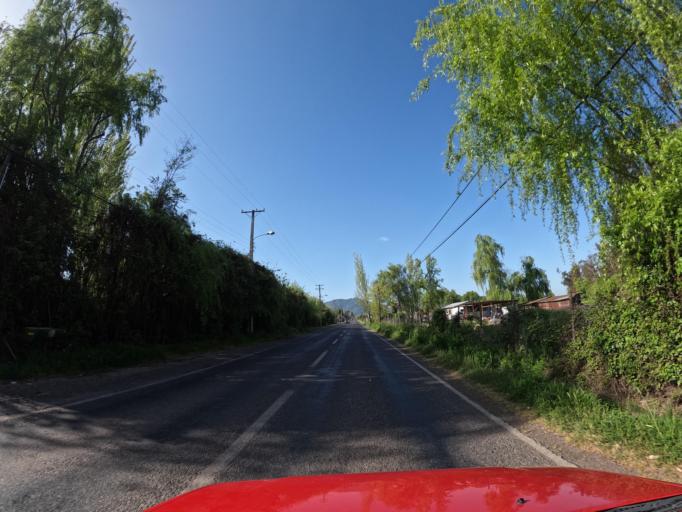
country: CL
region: Maule
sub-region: Provincia de Curico
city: Rauco
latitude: -34.8823
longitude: -71.2705
